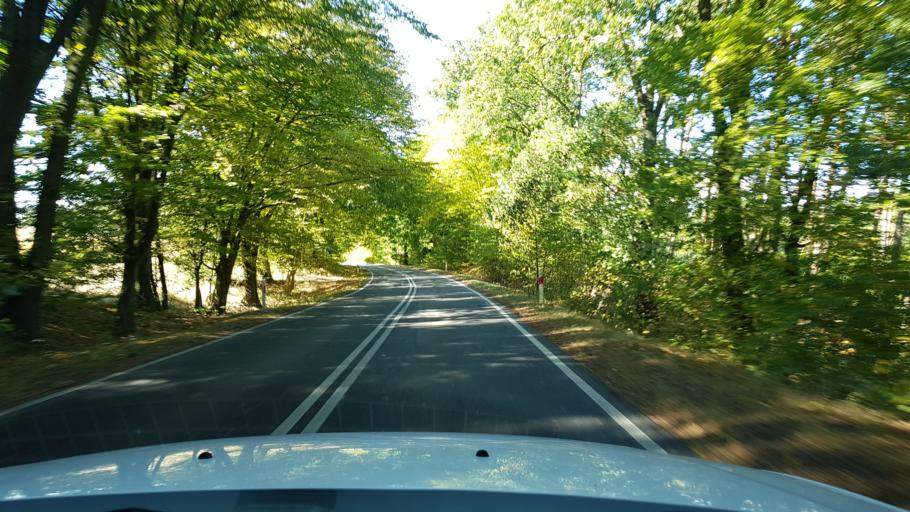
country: PL
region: West Pomeranian Voivodeship
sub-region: Powiat gryfinski
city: Gryfino
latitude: 53.1989
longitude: 14.5187
